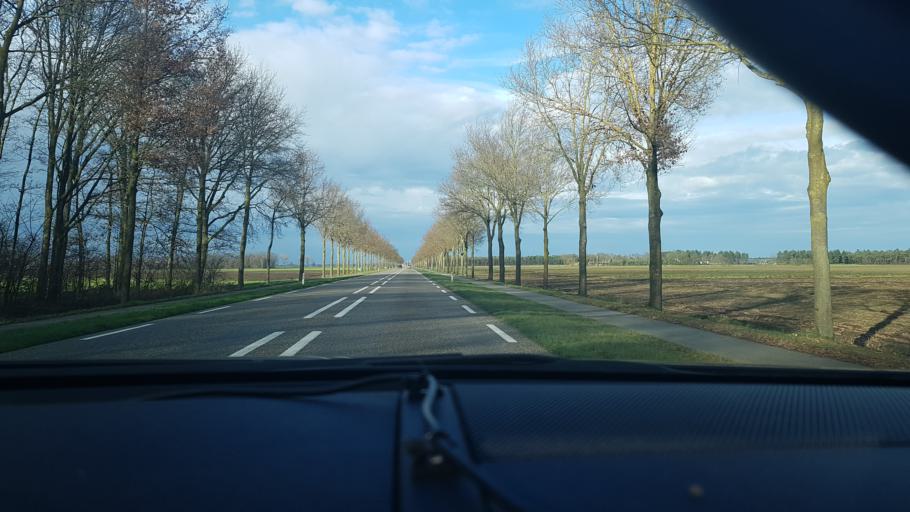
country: NL
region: Limburg
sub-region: Gemeente Peel en Maas
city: Maasbree
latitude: 51.3982
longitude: 5.9708
